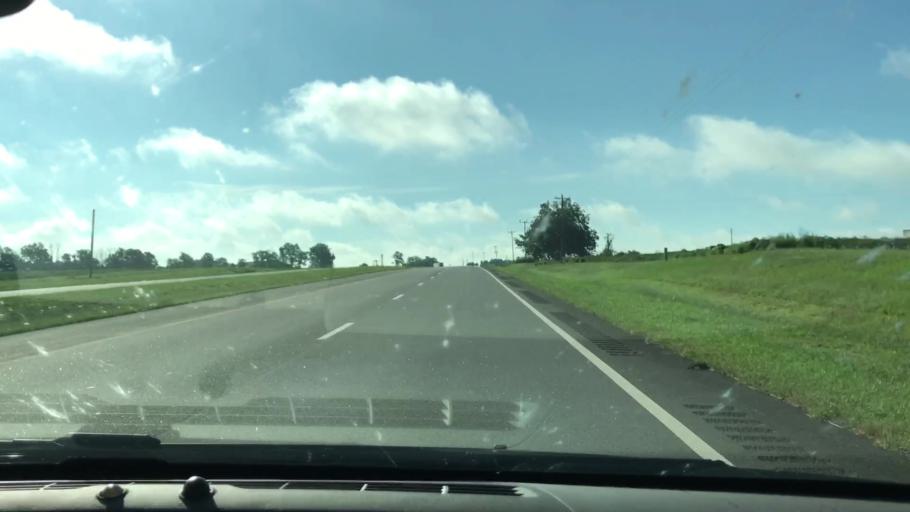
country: US
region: Georgia
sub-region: Terrell County
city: Dawson
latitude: 31.7384
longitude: -84.4073
